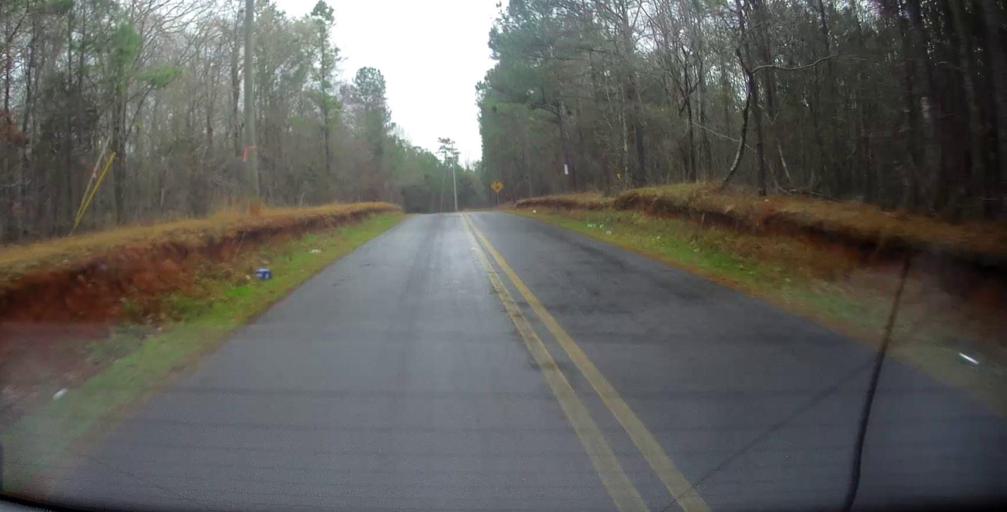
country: US
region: Georgia
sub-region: Monroe County
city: Forsyth
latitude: 33.0792
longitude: -83.8884
